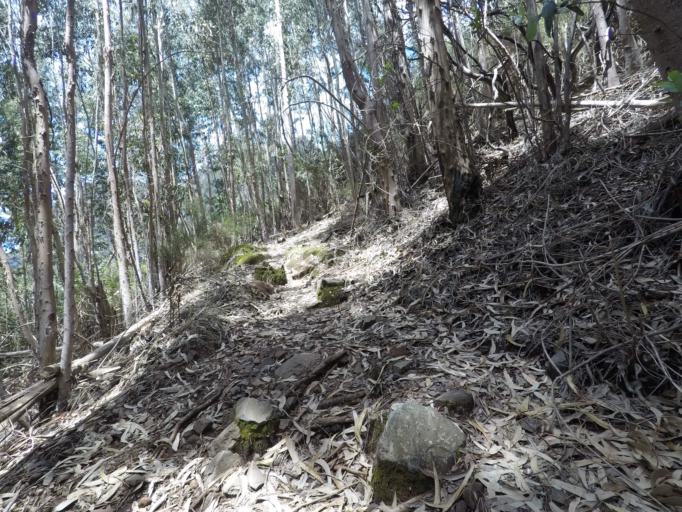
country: PT
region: Madeira
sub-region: Camara de Lobos
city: Curral das Freiras
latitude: 32.7527
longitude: -16.9725
